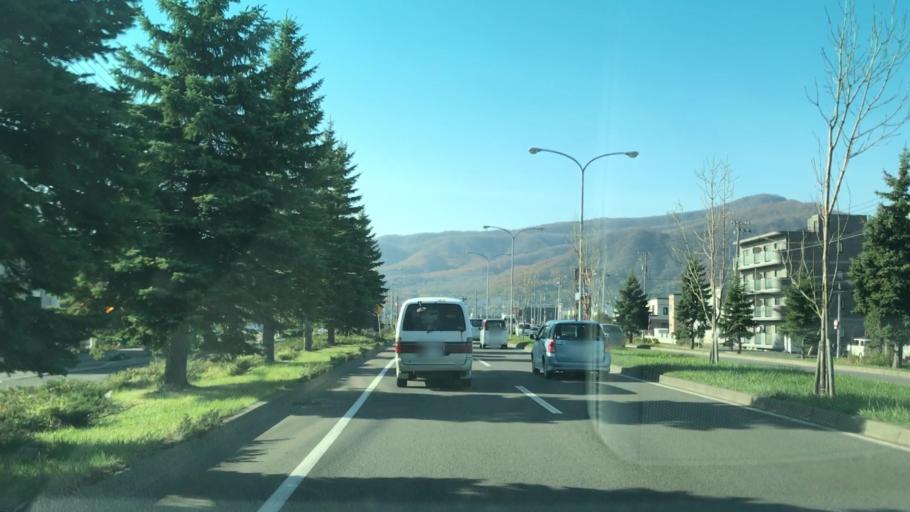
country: JP
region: Hokkaido
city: Sapporo
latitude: 43.1073
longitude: 141.2759
